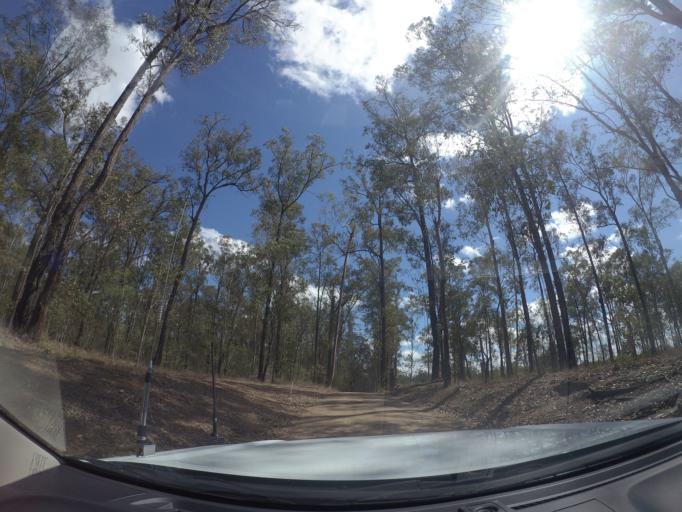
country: AU
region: Queensland
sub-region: Logan
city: North Maclean
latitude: -27.8259
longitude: 152.9684
